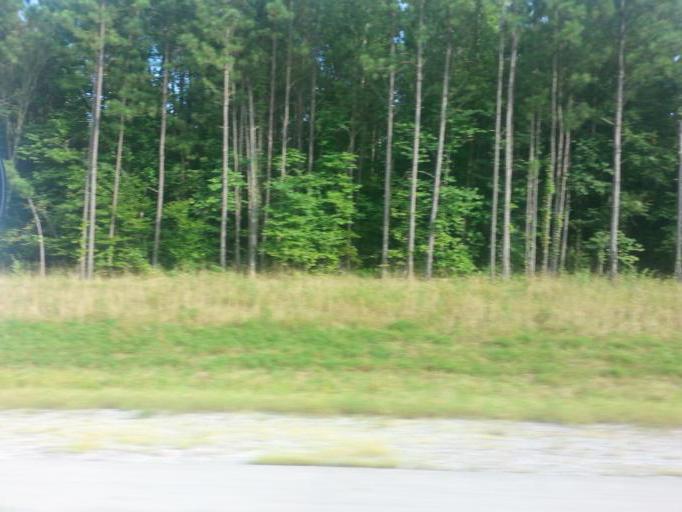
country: US
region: Tennessee
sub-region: Roane County
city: Oliver Springs
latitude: 35.9646
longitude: -84.3532
